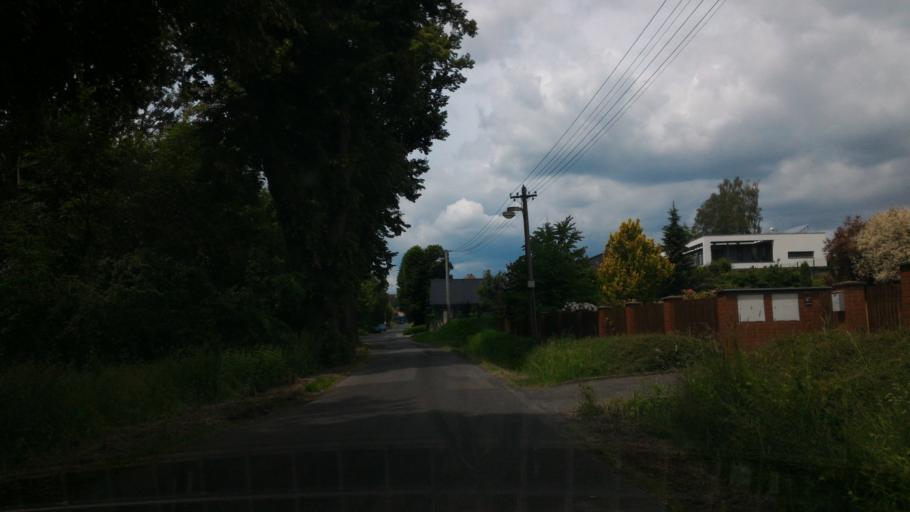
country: CZ
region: Ustecky
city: Varnsdorf
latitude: 50.9103
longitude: 14.6456
